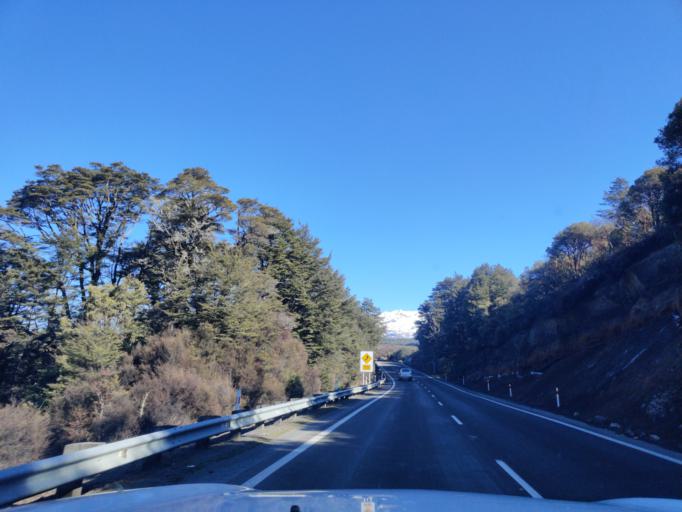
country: NZ
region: Waikato
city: Turangi
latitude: -39.2145
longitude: 175.7406
